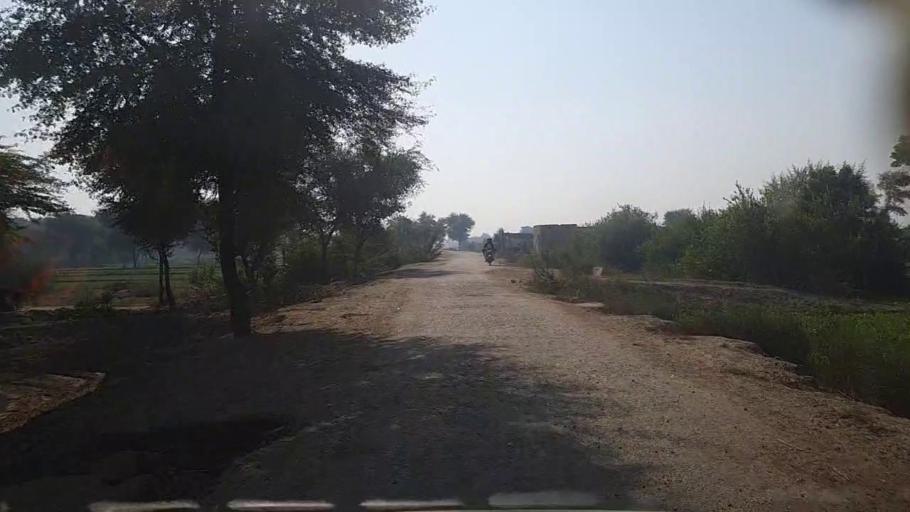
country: PK
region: Sindh
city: Kandiari
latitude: 26.9878
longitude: 68.4694
